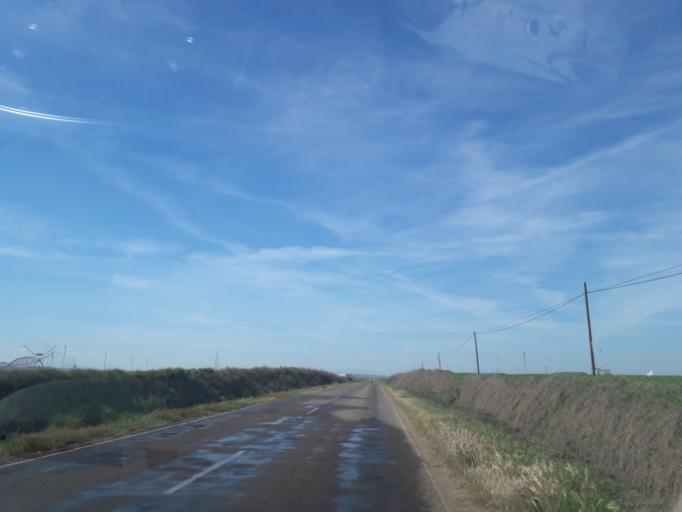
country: ES
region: Castille and Leon
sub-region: Provincia de Salamanca
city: Villoruela
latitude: 40.9948
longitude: -5.4027
